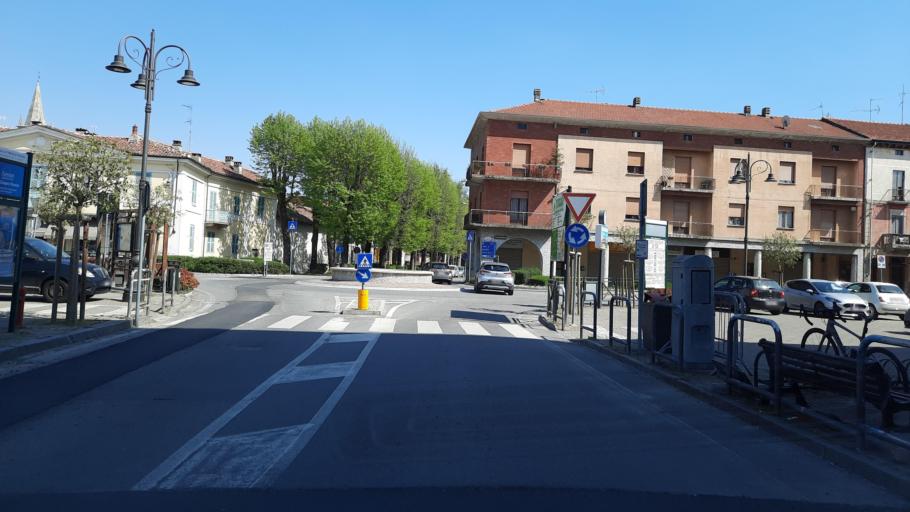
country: IT
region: Piedmont
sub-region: Provincia di Vercelli
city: Crescentino
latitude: 45.1905
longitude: 8.1017
